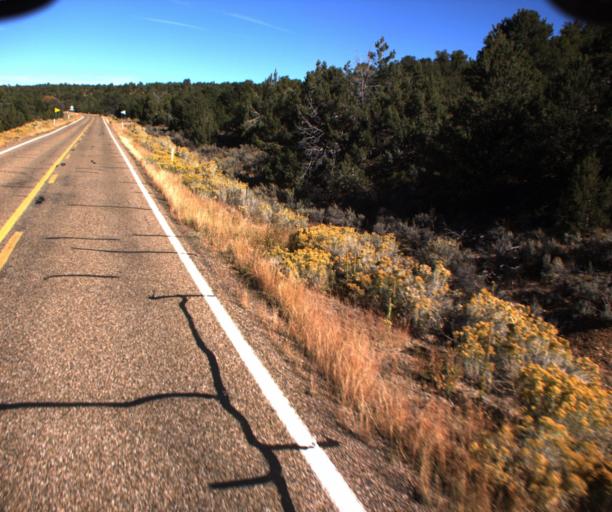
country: US
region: Arizona
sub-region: Coconino County
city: Fredonia
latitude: 36.7339
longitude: -112.0975
